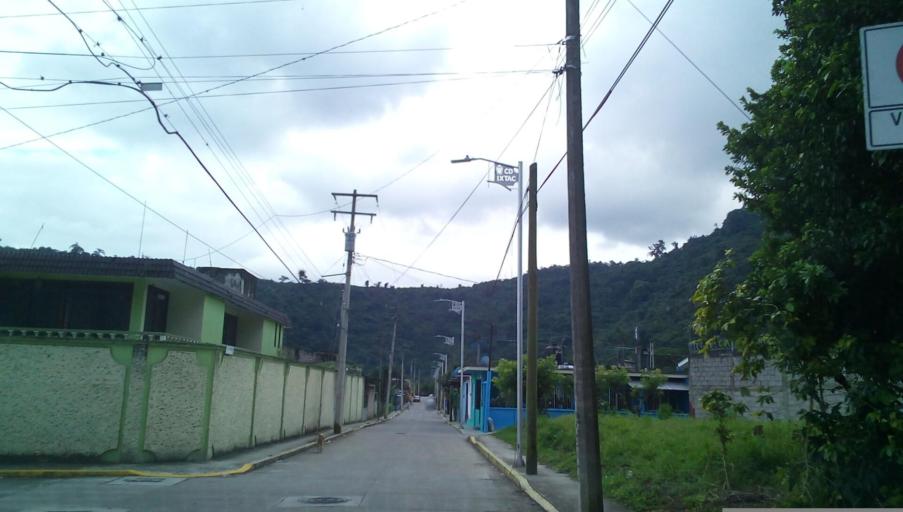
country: MX
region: Veracruz
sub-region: Ixtaczoquitlan
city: Buenavista
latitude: 18.8931
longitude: -97.0398
